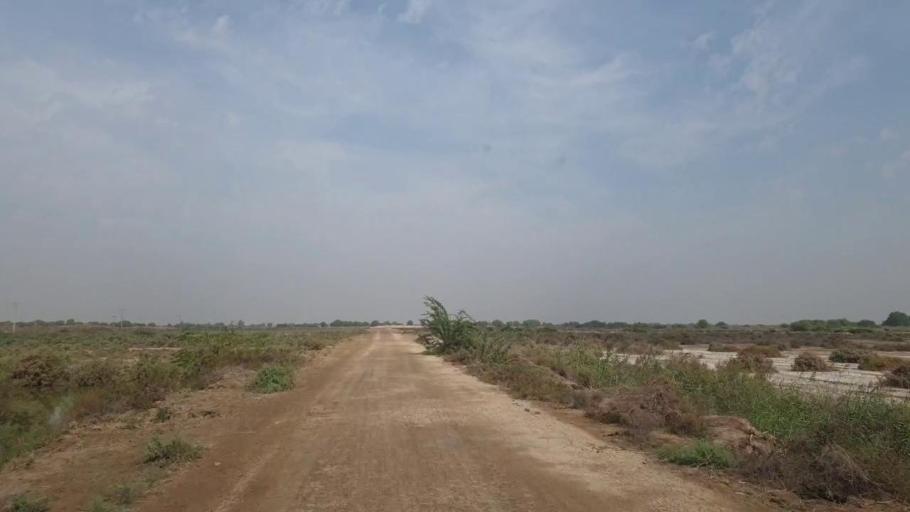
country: PK
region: Sindh
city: Rajo Khanani
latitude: 24.9932
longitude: 68.9951
